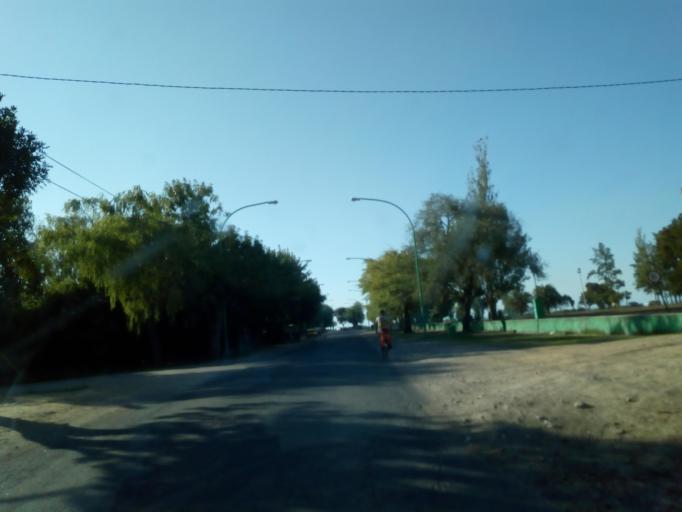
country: AR
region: Buenos Aires
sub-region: Partido de Ensenada
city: Ensenada
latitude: -34.8093
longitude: -57.9817
